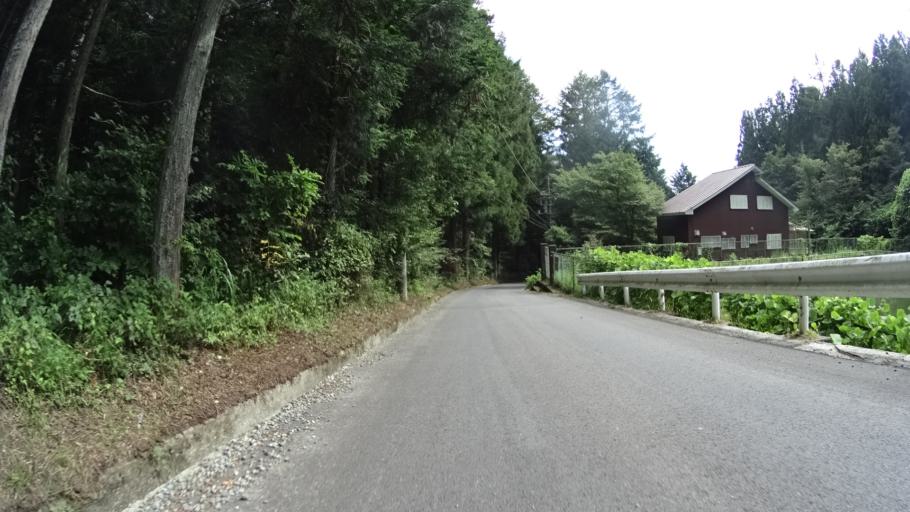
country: JP
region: Yamanashi
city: Nirasaki
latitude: 35.7870
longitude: 138.5329
